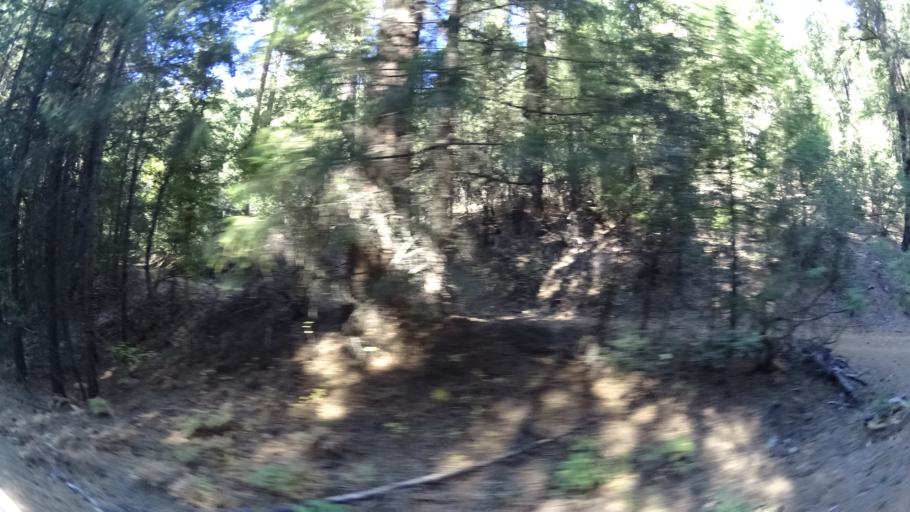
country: US
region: California
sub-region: Trinity County
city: Weaverville
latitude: 41.1996
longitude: -123.0708
